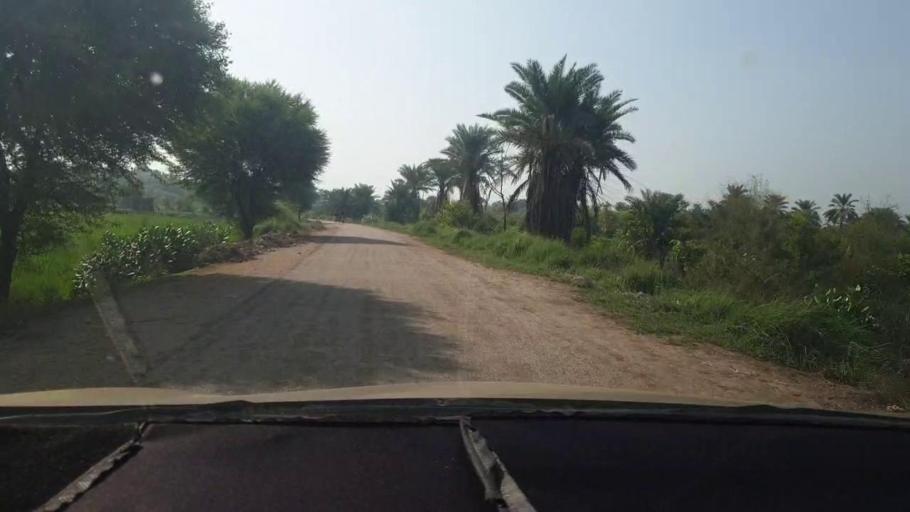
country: PK
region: Sindh
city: Kambar
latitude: 27.6108
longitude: 68.0911
